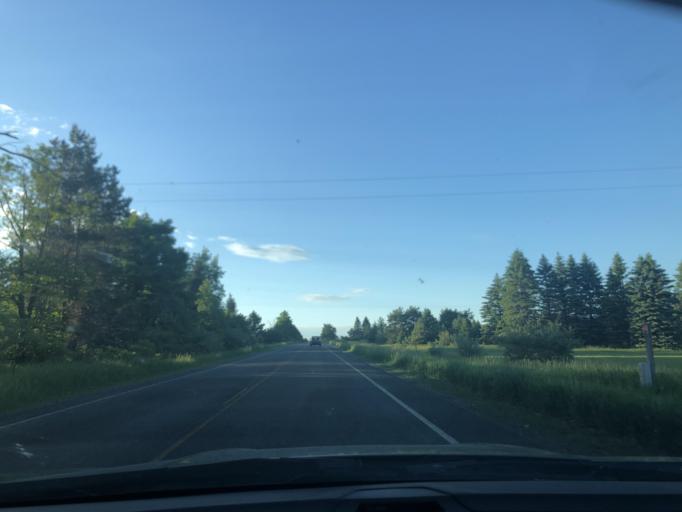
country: US
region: Michigan
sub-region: Missaukee County
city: Lake City
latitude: 44.4000
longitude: -85.0756
